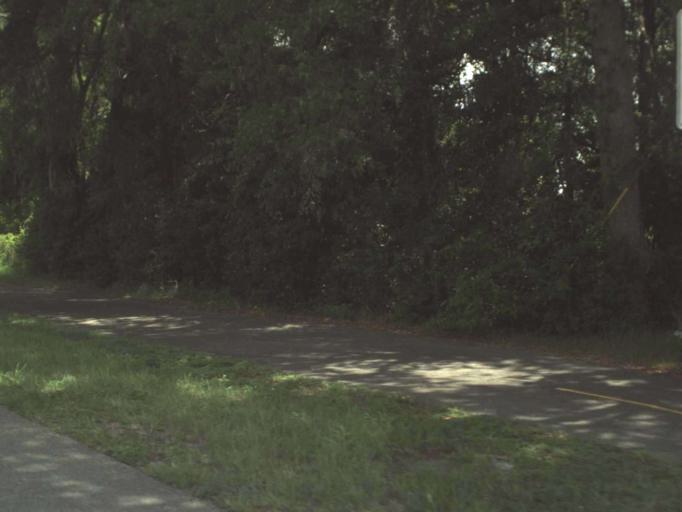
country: US
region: Florida
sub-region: Sumter County
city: Bushnell
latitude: 28.6686
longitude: -82.1043
